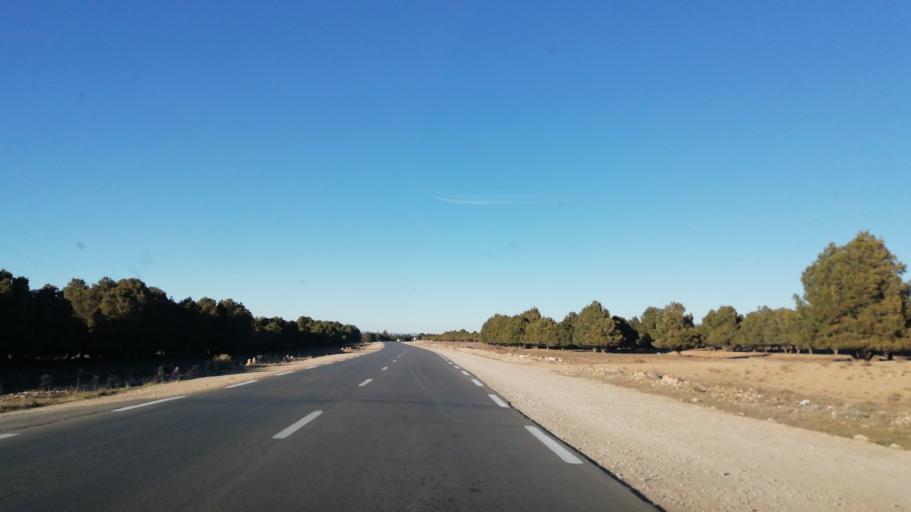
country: DZ
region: Tlemcen
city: Sebdou
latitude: 34.4541
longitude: -1.2753
